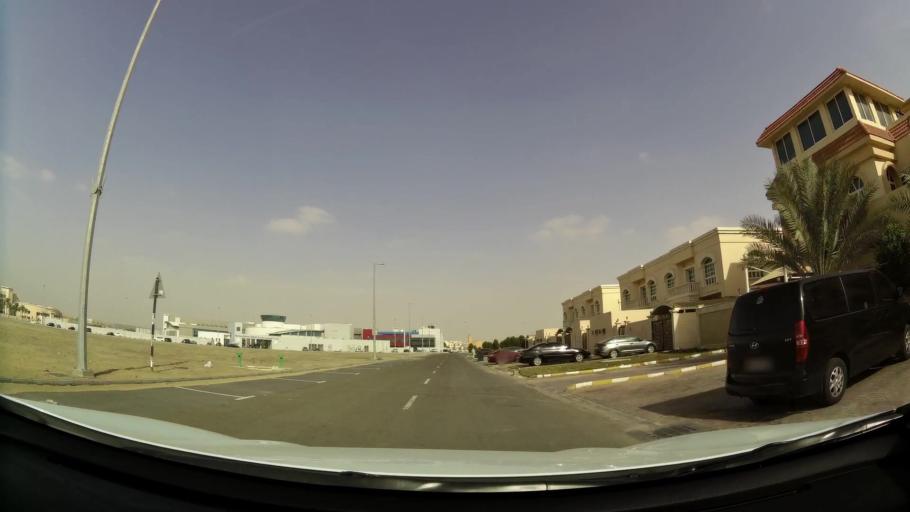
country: AE
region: Abu Dhabi
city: Abu Dhabi
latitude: 24.4178
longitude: 54.5962
